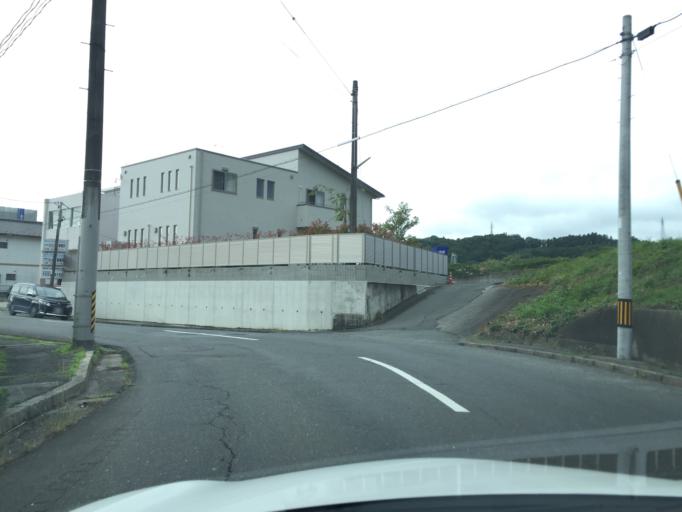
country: JP
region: Fukushima
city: Iwaki
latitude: 37.0511
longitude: 140.8830
